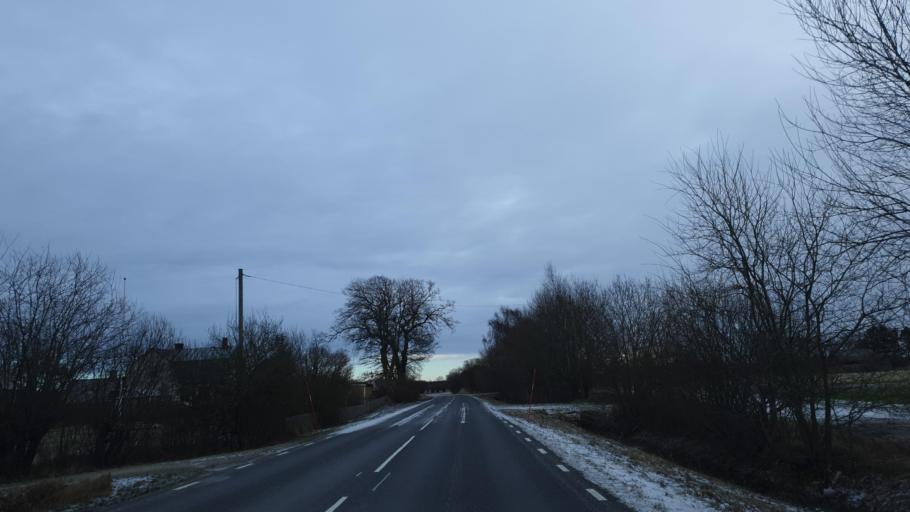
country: SE
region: Gotland
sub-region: Gotland
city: Slite
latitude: 57.4196
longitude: 18.8688
